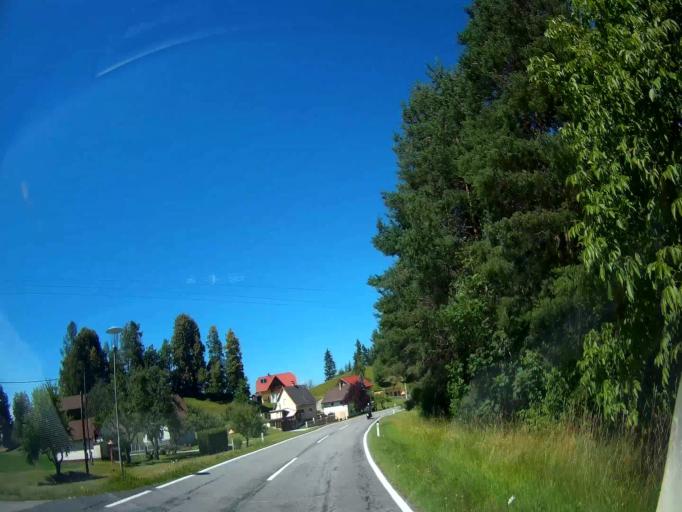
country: AT
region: Carinthia
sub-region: Politischer Bezirk Volkermarkt
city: Gallizien
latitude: 46.5474
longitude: 14.4705
